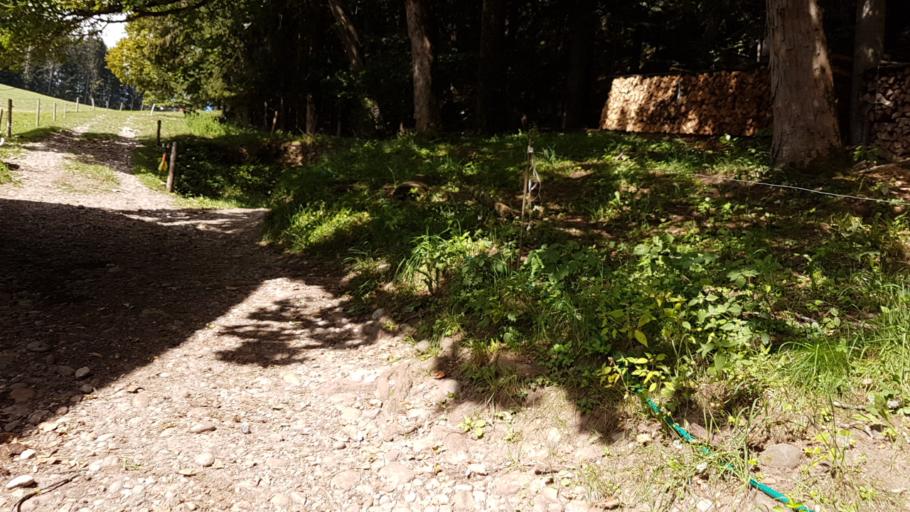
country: CH
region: Bern
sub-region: Thun District
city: Buchholterberg
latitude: 46.8300
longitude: 7.6767
